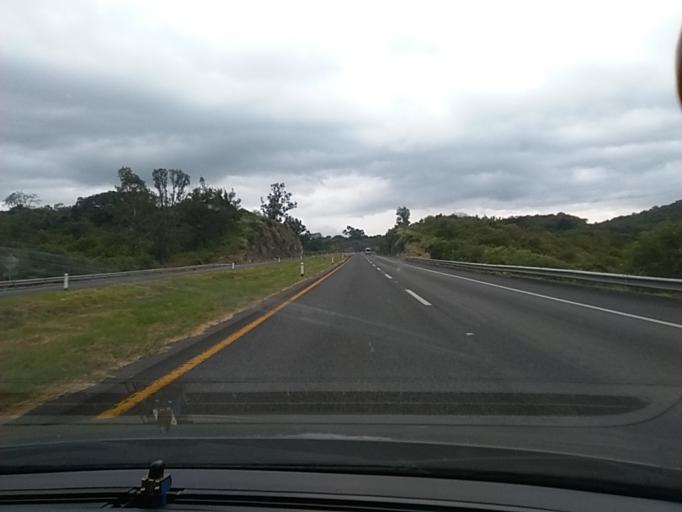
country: MX
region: Jalisco
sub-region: Zapotlan del Rey
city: Zapotlan del Rey
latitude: 20.5180
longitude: -102.9828
